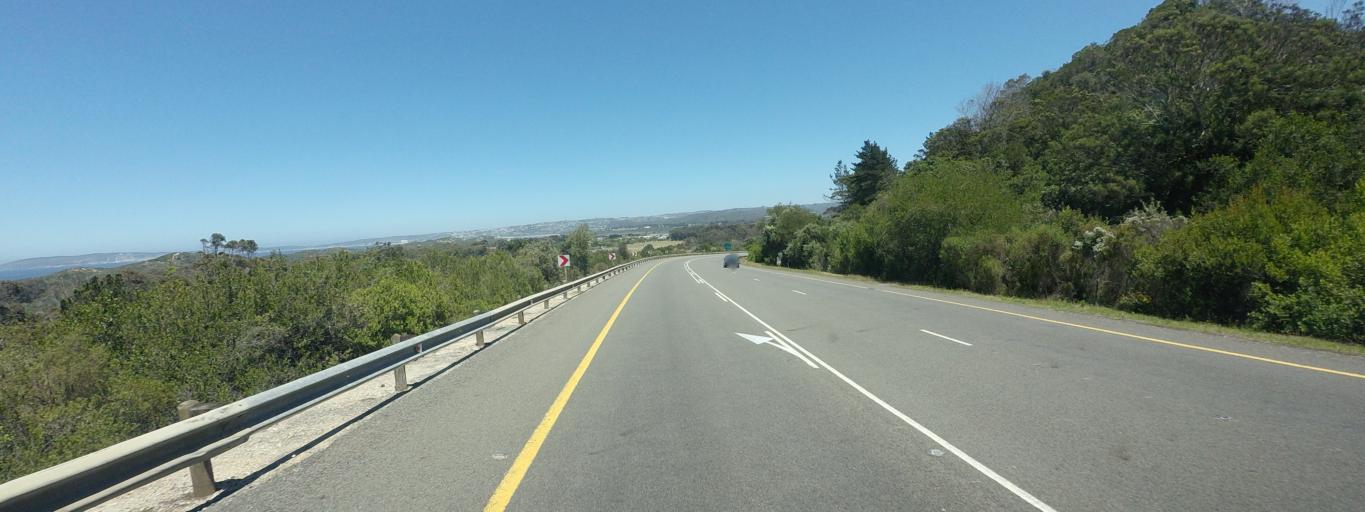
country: ZA
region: Western Cape
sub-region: Eden District Municipality
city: Plettenberg Bay
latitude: -34.0066
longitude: 23.4163
